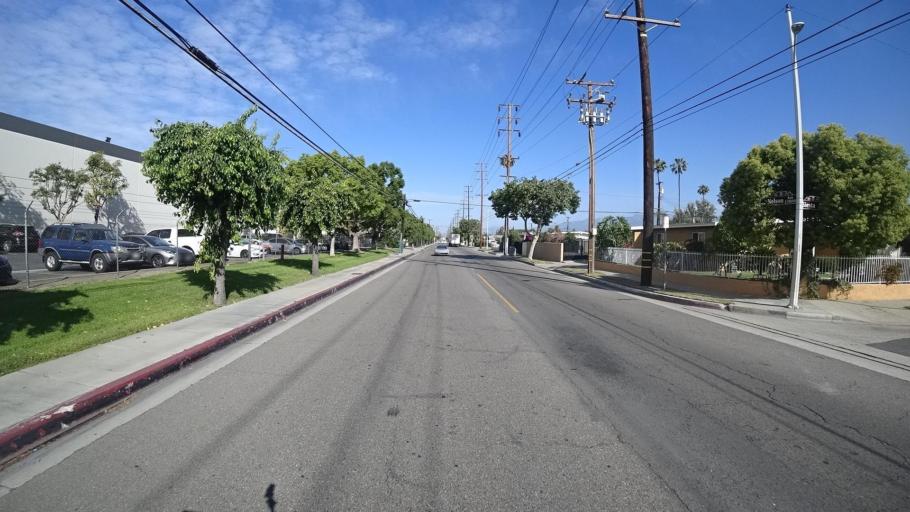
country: US
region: California
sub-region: Los Angeles County
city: Avocado Heights
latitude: 34.0452
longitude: -117.9834
